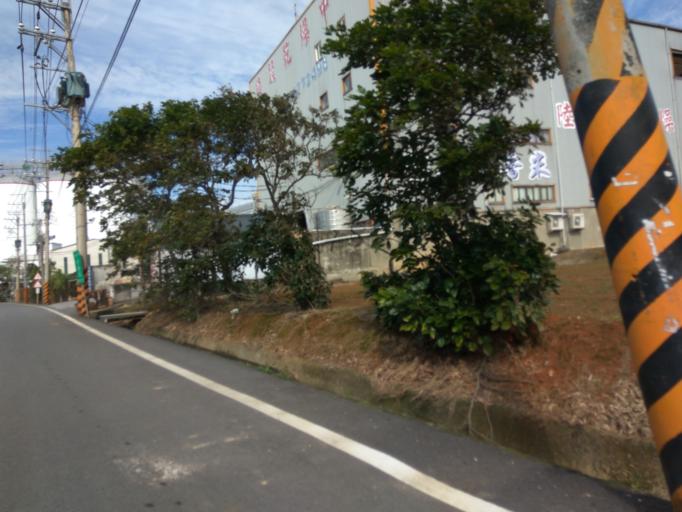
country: TW
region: Taiwan
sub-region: Hsinchu
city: Zhubei
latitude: 24.9949
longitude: 121.0940
